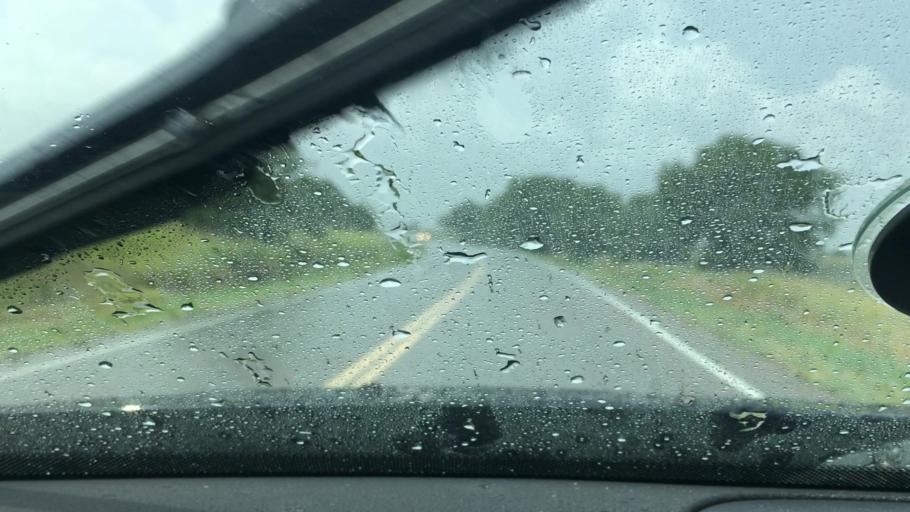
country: US
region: Oklahoma
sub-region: Johnston County
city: Tishomingo
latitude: 34.1640
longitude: -96.7071
